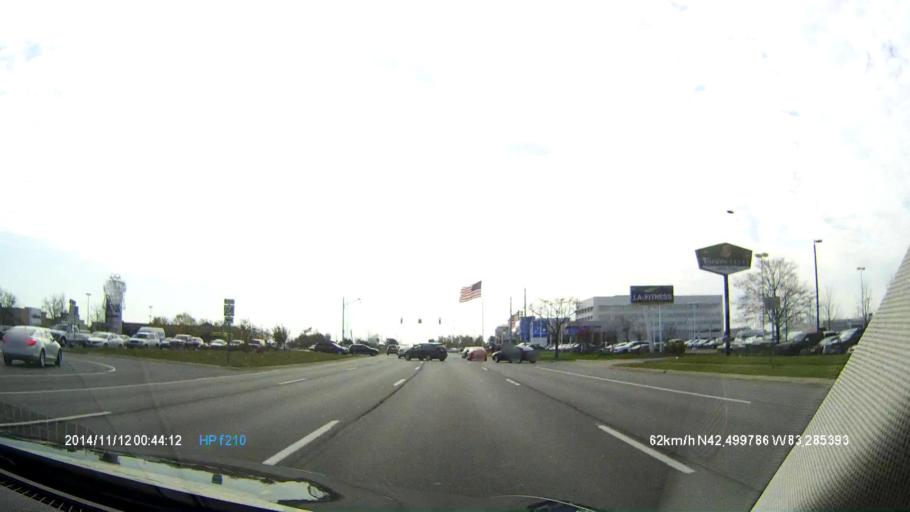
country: US
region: Michigan
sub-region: Oakland County
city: Bingham Farms
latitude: 42.4995
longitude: -83.2854
